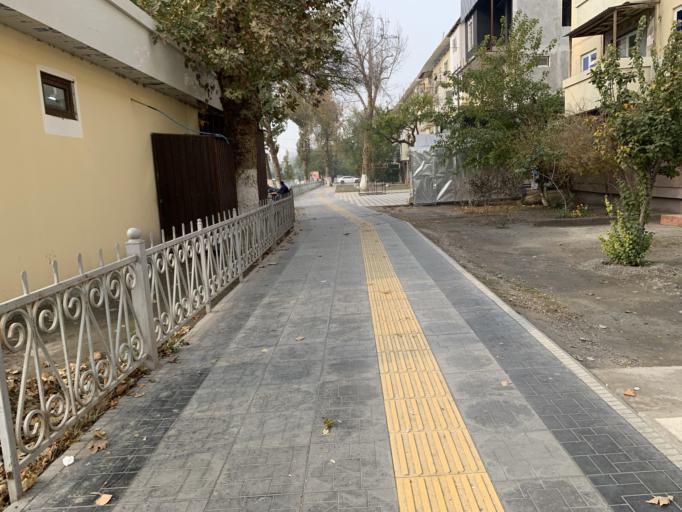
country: UZ
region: Fergana
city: Qo`qon
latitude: 40.5443
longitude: 70.9333
